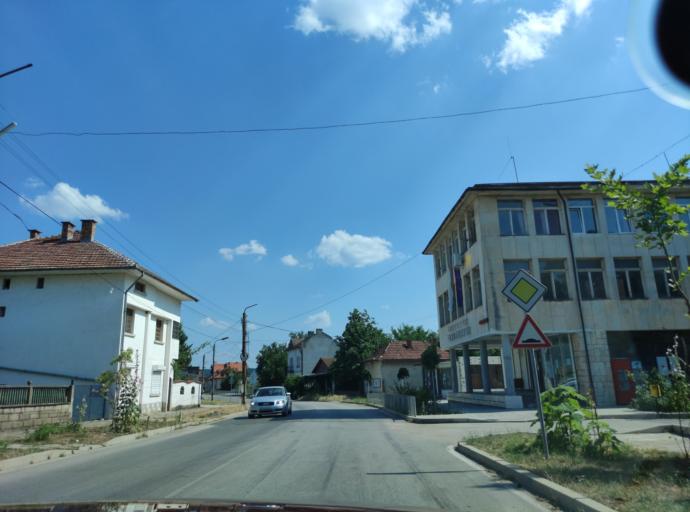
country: BG
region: Pleven
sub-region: Obshtina Cherven Bryag
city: Cherven Bryag
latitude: 43.3281
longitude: 24.0672
